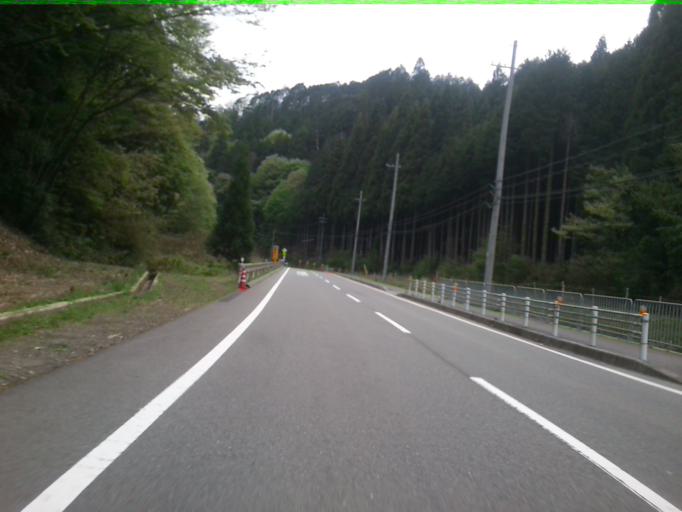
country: JP
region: Kyoto
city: Kameoka
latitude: 34.9598
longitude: 135.5559
